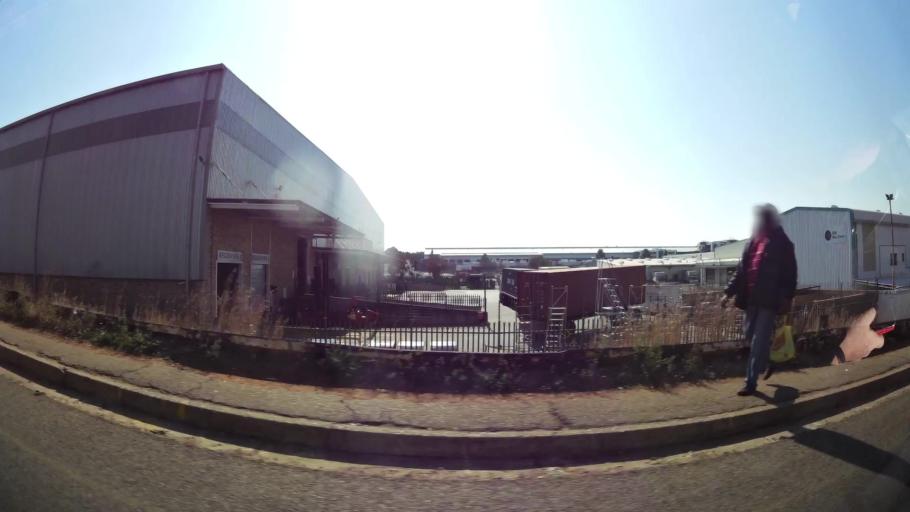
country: ZA
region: Gauteng
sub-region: Ekurhuleni Metropolitan Municipality
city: Boksburg
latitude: -26.1677
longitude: 28.2312
